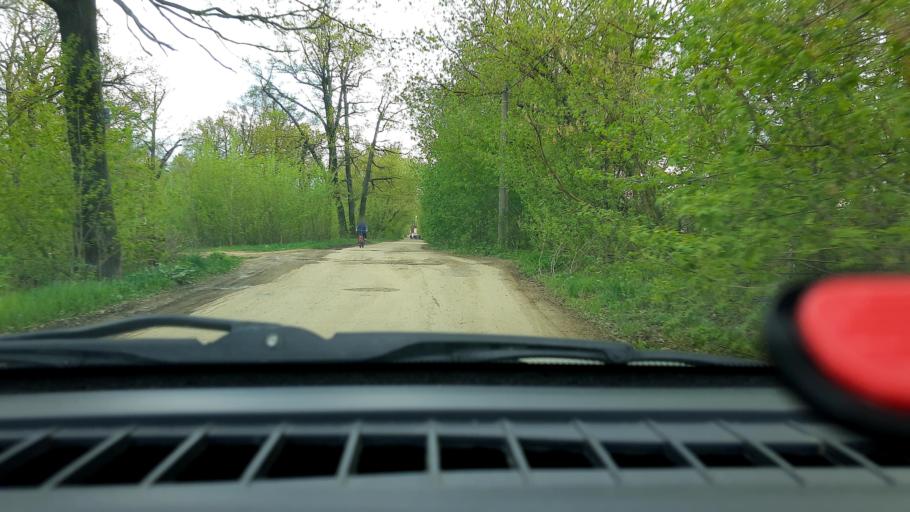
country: RU
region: Nizjnij Novgorod
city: Neklyudovo
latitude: 56.3842
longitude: 43.8365
